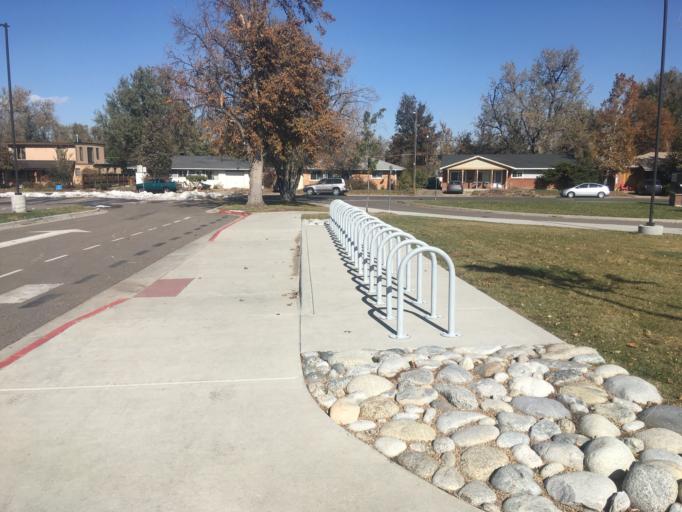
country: US
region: Colorado
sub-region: Boulder County
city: Boulder
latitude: 39.9908
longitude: -105.2492
